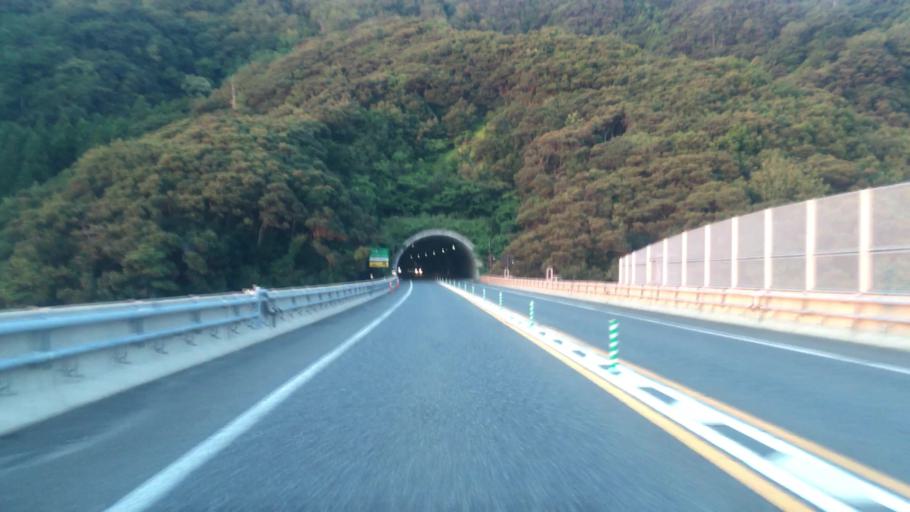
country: JP
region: Tottori
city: Tottori
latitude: 35.5999
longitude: 134.3736
